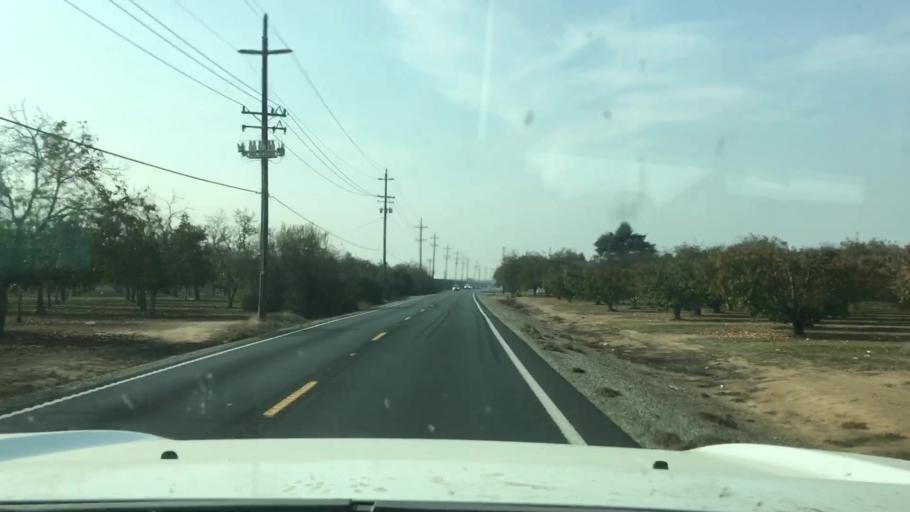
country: US
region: California
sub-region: San Joaquin County
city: Linden
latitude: 38.0120
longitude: -121.1110
